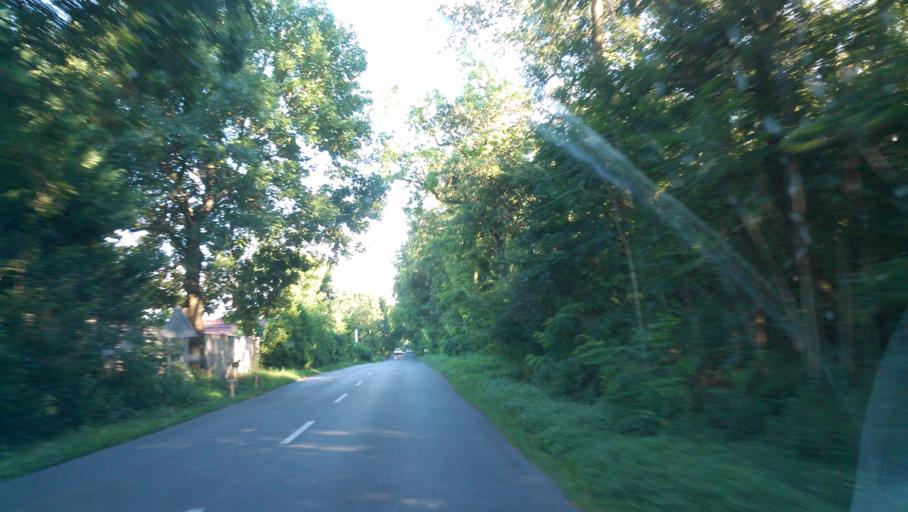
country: SK
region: Bratislavsky
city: Svaty Jur
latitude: 48.1825
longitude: 17.2681
